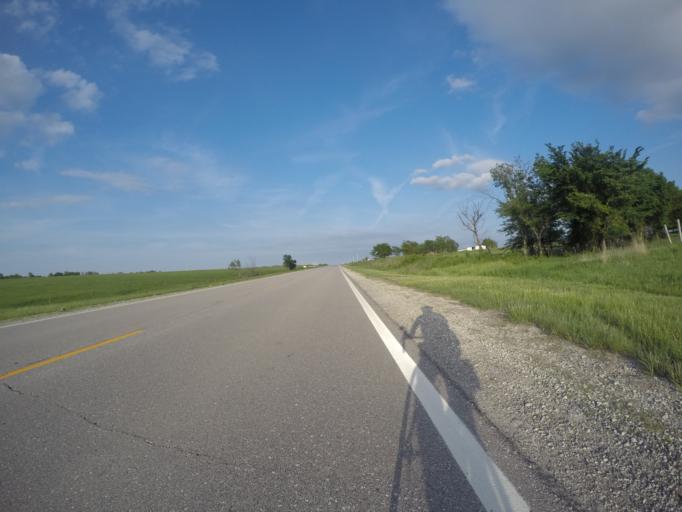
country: US
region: Kansas
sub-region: Pottawatomie County
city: Westmoreland
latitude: 39.4283
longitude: -96.5608
